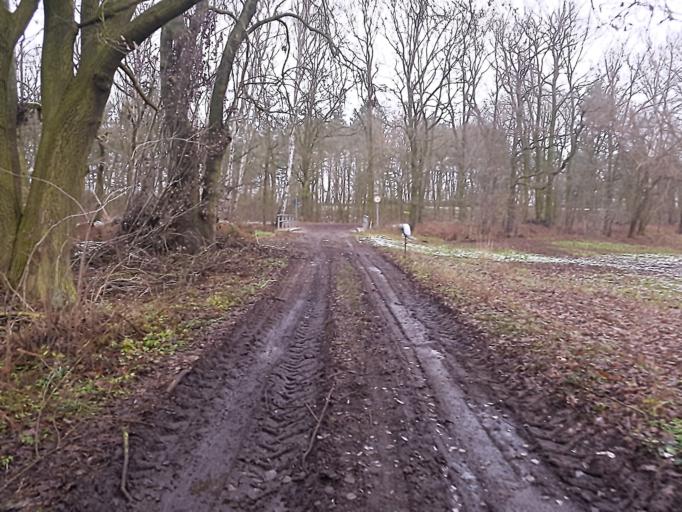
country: DE
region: Brandenburg
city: Lubbenau
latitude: 51.8248
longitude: 13.9100
